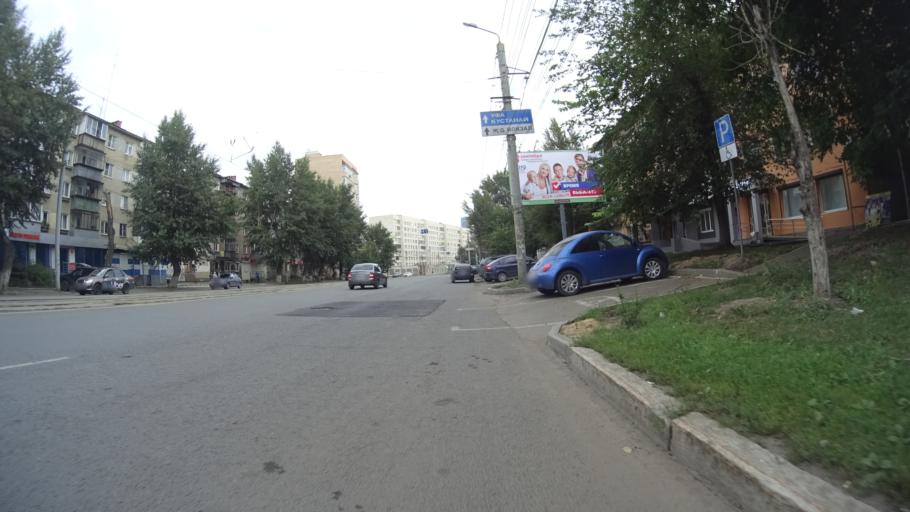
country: RU
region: Chelyabinsk
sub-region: Gorod Chelyabinsk
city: Chelyabinsk
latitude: 55.1511
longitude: 61.4105
